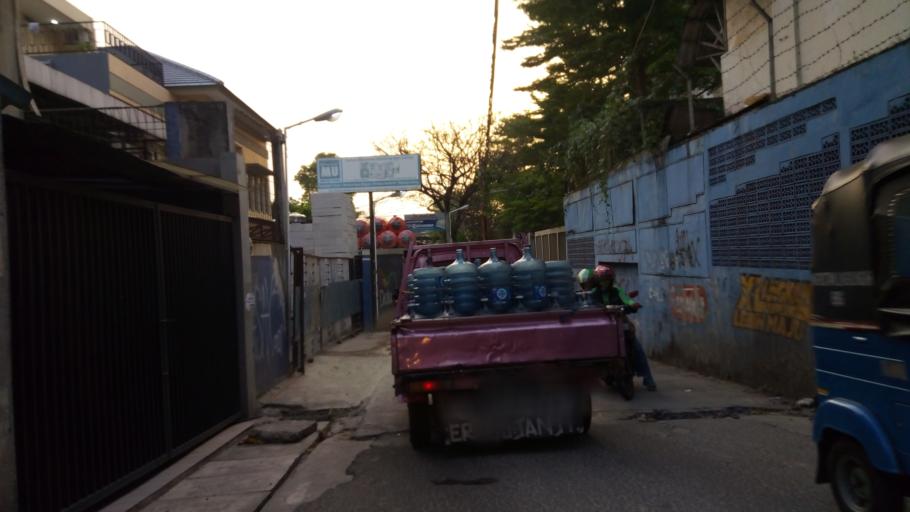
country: ID
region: Jakarta Raya
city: Jakarta
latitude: -6.2468
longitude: 106.7895
